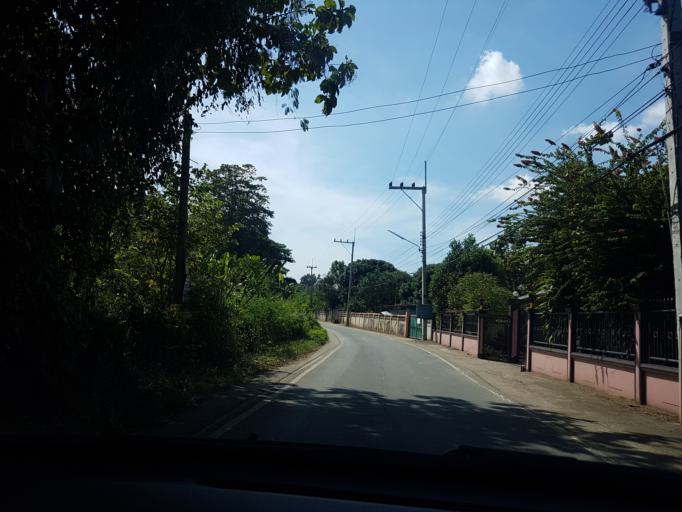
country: TH
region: Lampang
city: Ko Kha
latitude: 18.2099
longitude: 99.4031
